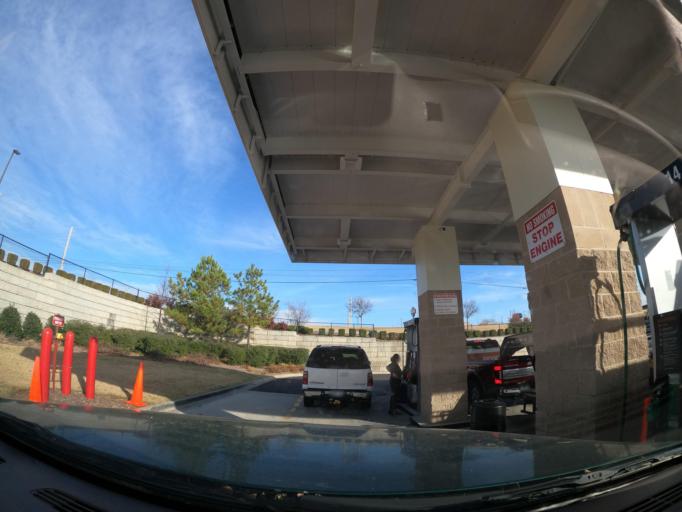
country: US
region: Oklahoma
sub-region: Tulsa County
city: Bixby
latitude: 36.0151
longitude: -95.8872
